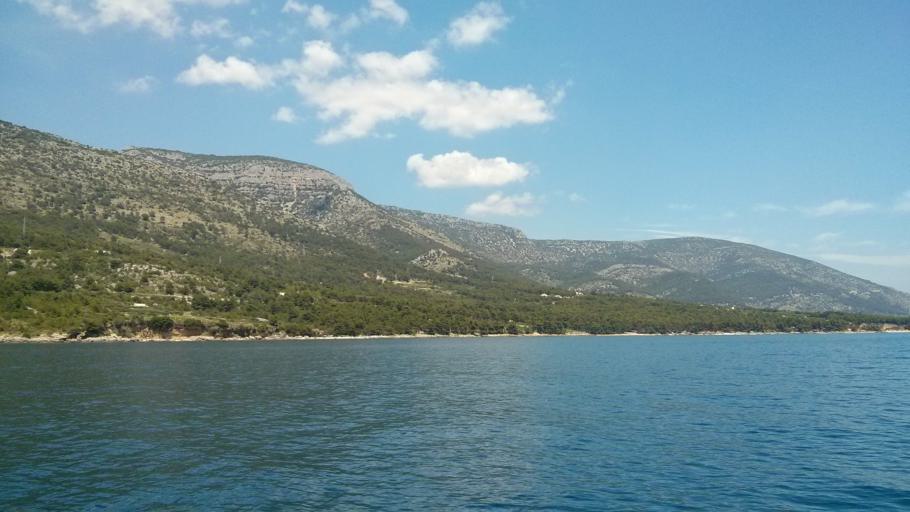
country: HR
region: Splitsko-Dalmatinska
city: Bol
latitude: 43.2565
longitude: 16.6165
